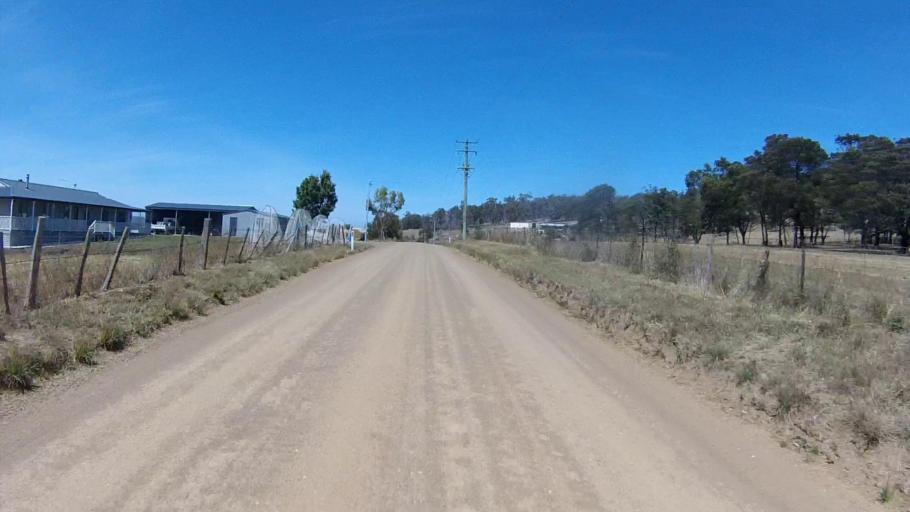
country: AU
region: Tasmania
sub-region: Sorell
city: Sorell
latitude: -42.7888
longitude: 147.6382
